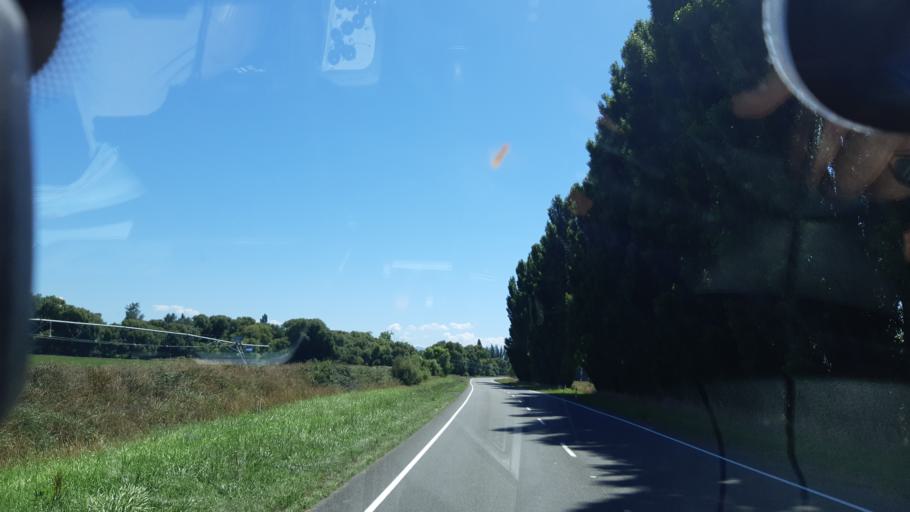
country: NZ
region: Canterbury
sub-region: Kaikoura District
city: Kaikoura
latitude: -42.7327
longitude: 173.2741
